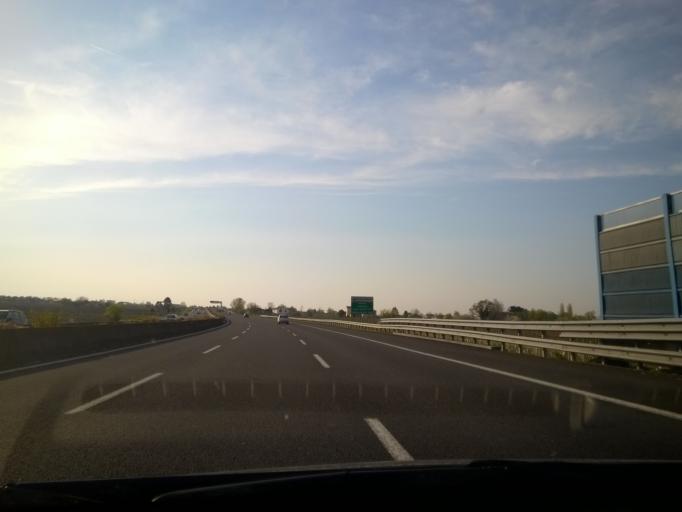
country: IT
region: Emilia-Romagna
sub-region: Provincia di Ravenna
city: Granarolo
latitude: 44.3175
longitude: 11.9211
